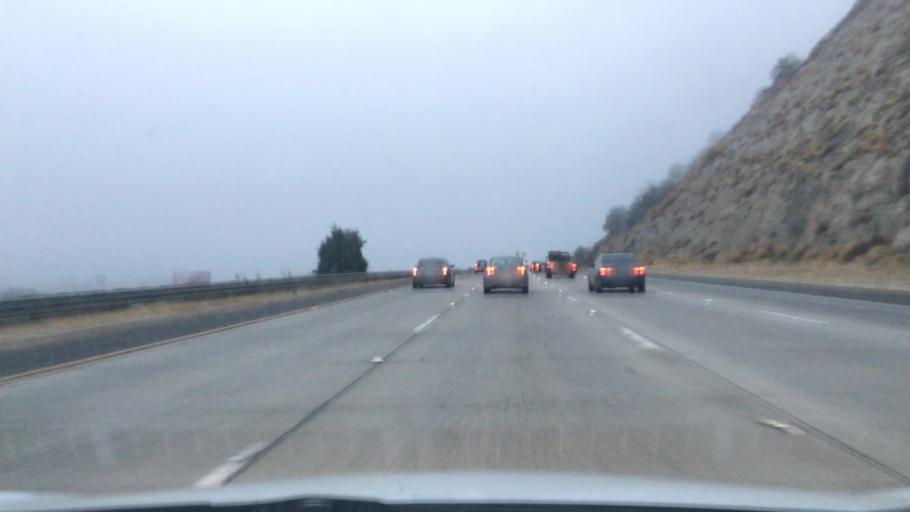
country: US
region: California
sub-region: San Diego County
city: Rainbow
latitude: 33.4201
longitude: -117.1551
